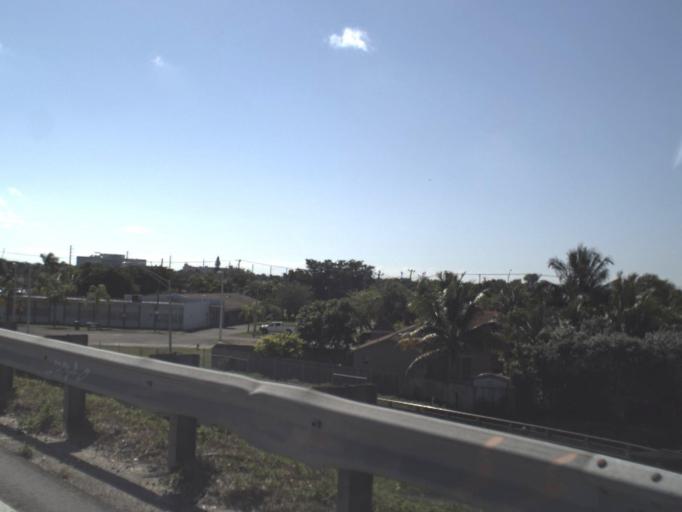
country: US
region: Florida
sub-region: Miami-Dade County
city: South Miami Heights
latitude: 25.5974
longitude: -80.3749
